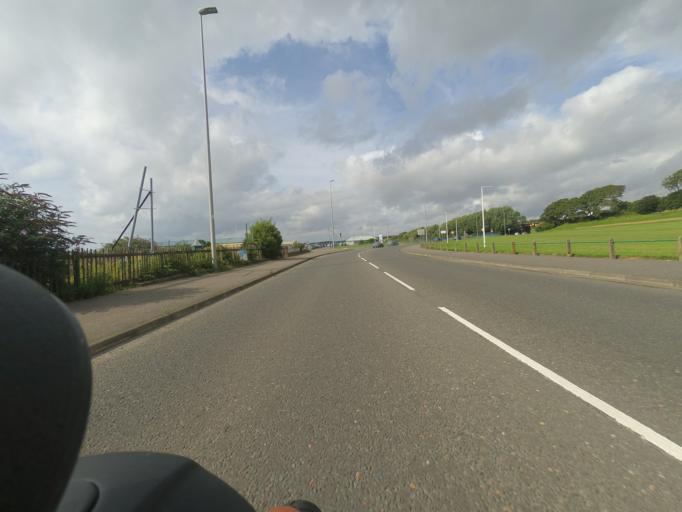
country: GB
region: Scotland
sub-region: Angus
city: Arbroath
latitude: 56.5526
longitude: -2.5952
